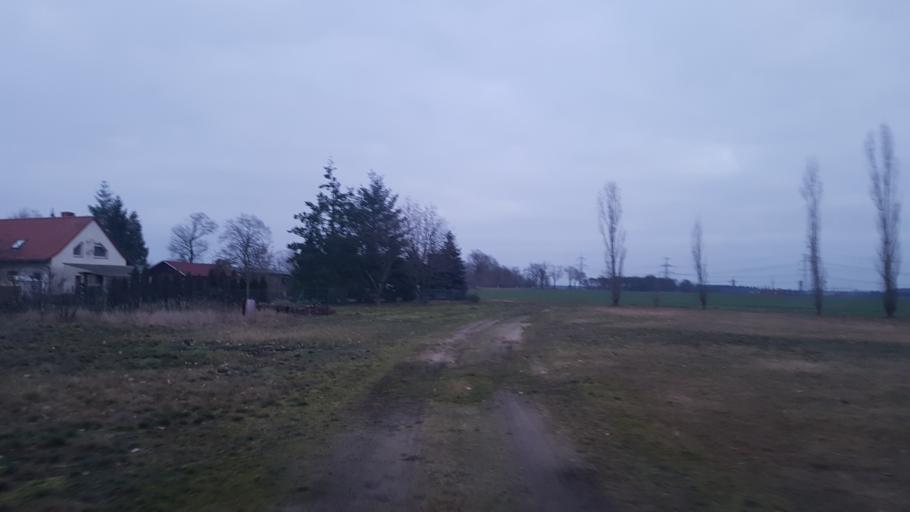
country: DE
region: Saxony-Anhalt
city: Holzdorf
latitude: 51.8355
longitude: 13.1467
